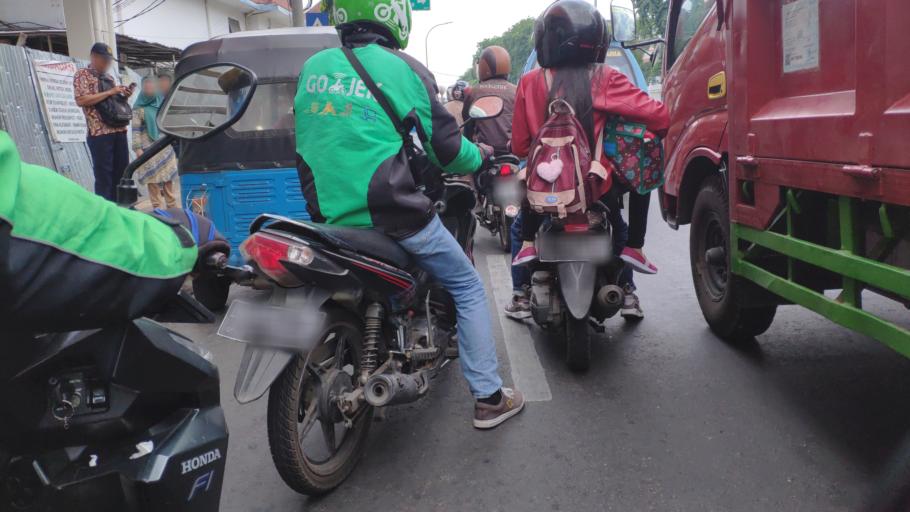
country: ID
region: Jakarta Raya
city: Jakarta
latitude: -6.2154
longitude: 106.8698
